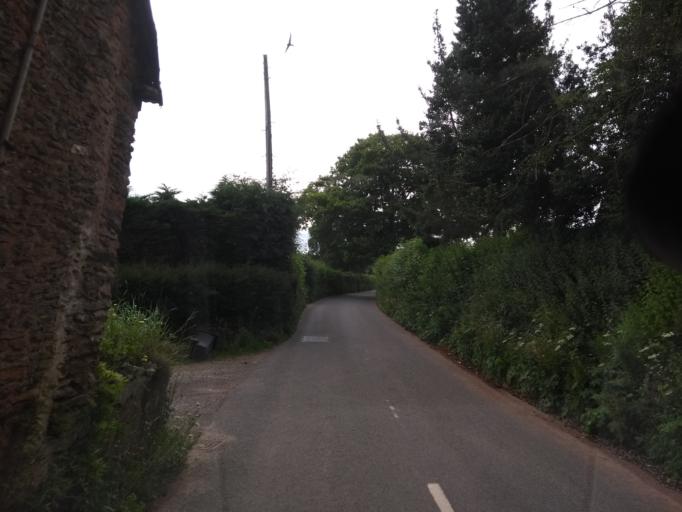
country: GB
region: England
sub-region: Somerset
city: Williton
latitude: 51.1058
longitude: -3.3086
